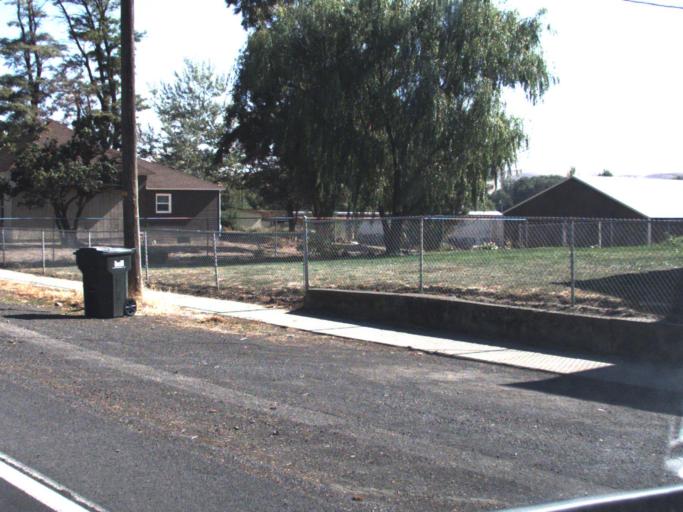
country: US
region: Washington
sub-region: Walla Walla County
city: Waitsburg
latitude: 46.2996
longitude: -118.3107
